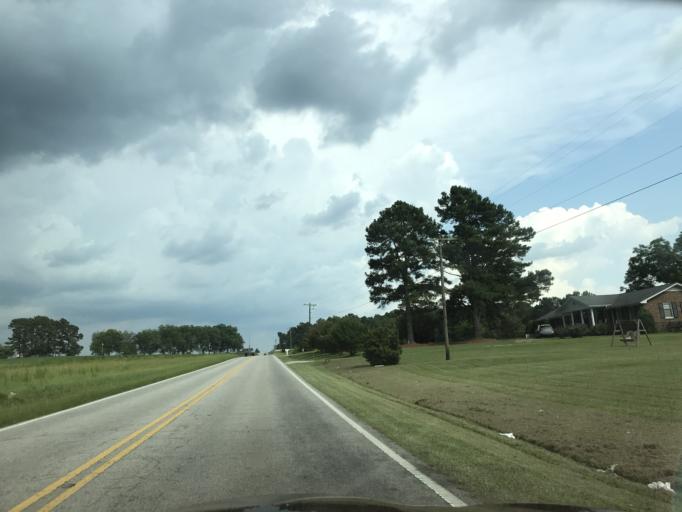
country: US
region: North Carolina
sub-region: Johnston County
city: Four Oaks
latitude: 35.5130
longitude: -78.5316
